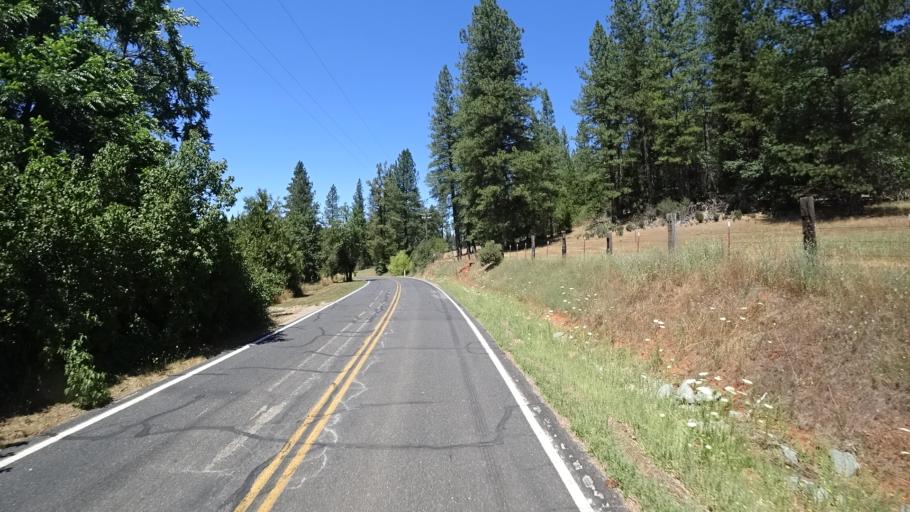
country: US
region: California
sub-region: Calaveras County
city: Mountain Ranch
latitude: 38.3224
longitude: -120.5203
